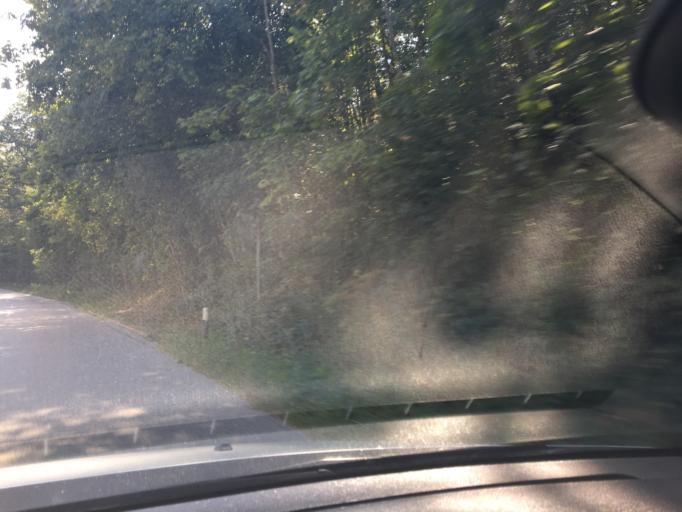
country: DE
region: Bavaria
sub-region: Upper Bavaria
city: Altoetting
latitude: 48.2419
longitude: 12.6701
